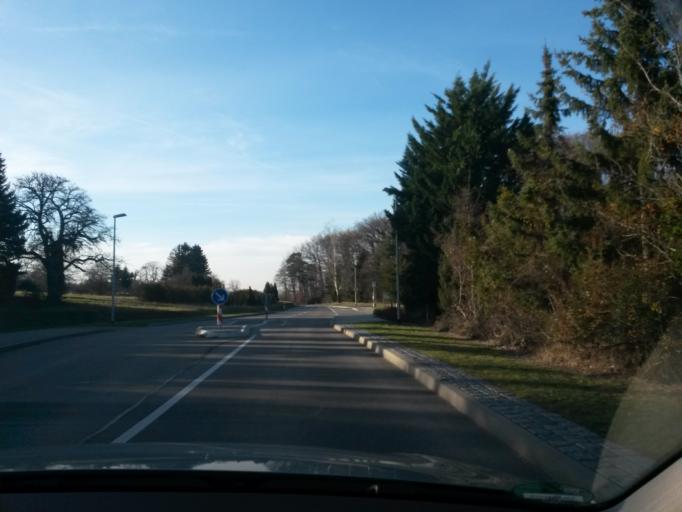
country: DE
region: Baden-Wuerttemberg
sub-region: Karlsruhe Region
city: Birkenfeld
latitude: 48.8705
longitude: 8.6215
